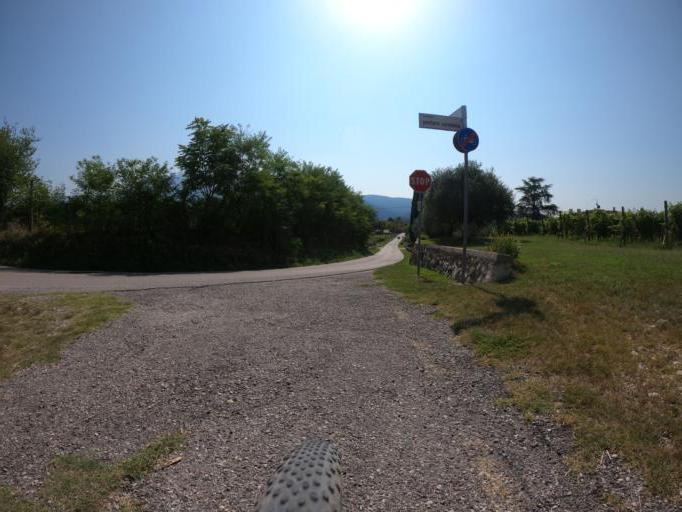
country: IT
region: Veneto
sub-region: Provincia di Verona
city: Caprino Veronese
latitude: 45.5867
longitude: 10.7899
